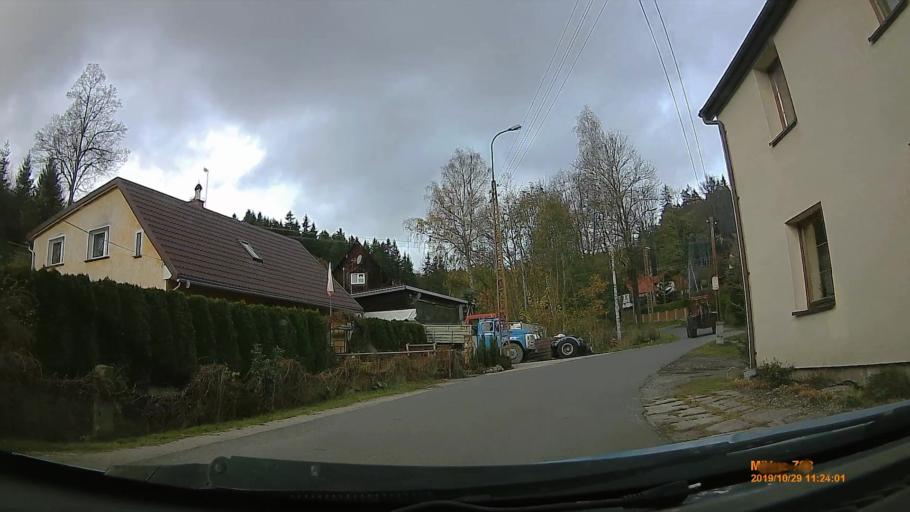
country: PL
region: Lower Silesian Voivodeship
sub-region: Powiat klodzki
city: Szczytna
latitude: 50.4407
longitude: 16.4234
